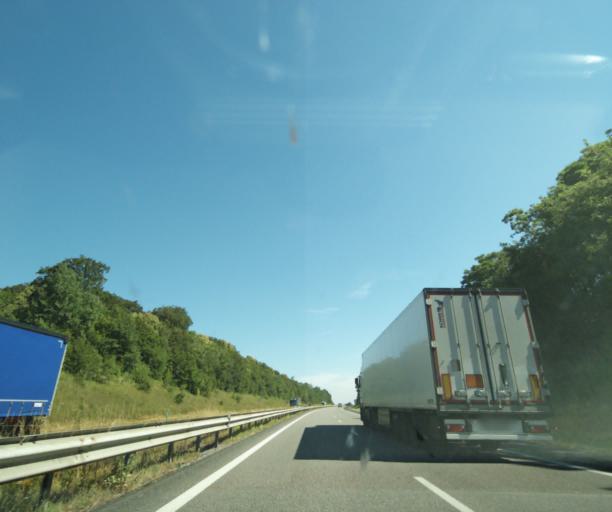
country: FR
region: Lorraine
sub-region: Departement des Vosges
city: Bulgneville
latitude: 48.2438
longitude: 5.8615
